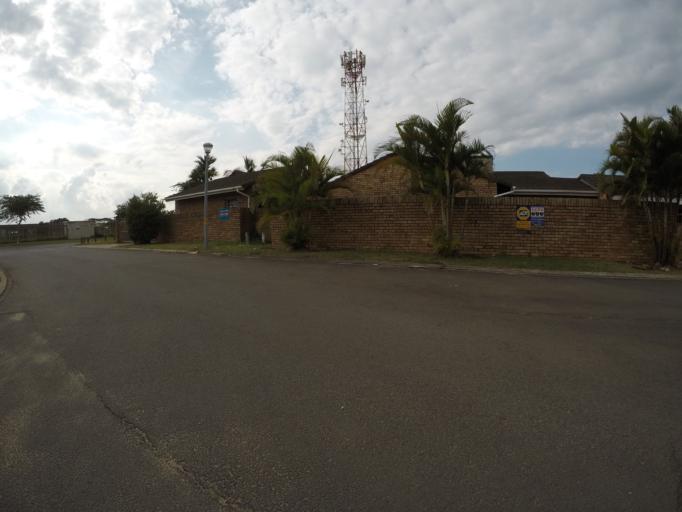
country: ZA
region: KwaZulu-Natal
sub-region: uThungulu District Municipality
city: Richards Bay
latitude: -28.7371
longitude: 32.0840
